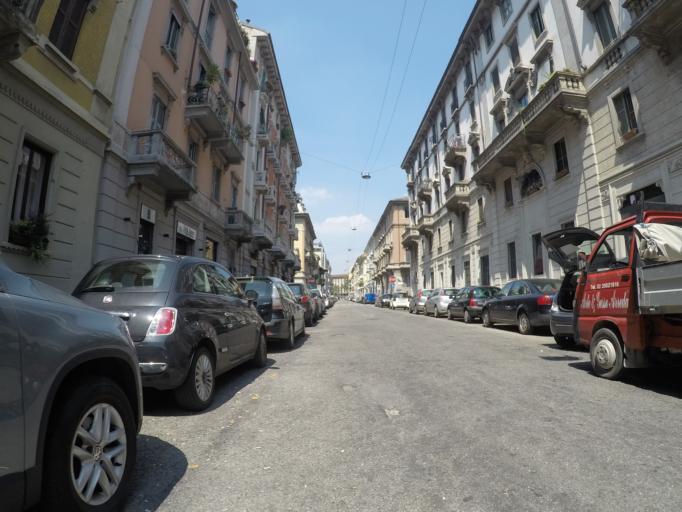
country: IT
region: Lombardy
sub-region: Citta metropolitana di Milano
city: Milano
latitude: 45.4688
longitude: 9.2159
